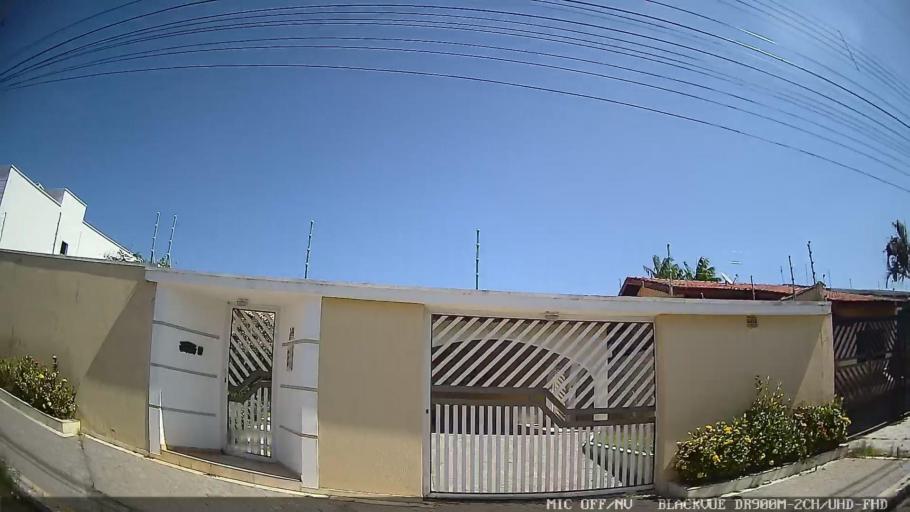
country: BR
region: Sao Paulo
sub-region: Peruibe
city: Peruibe
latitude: -24.2921
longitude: -46.9711
